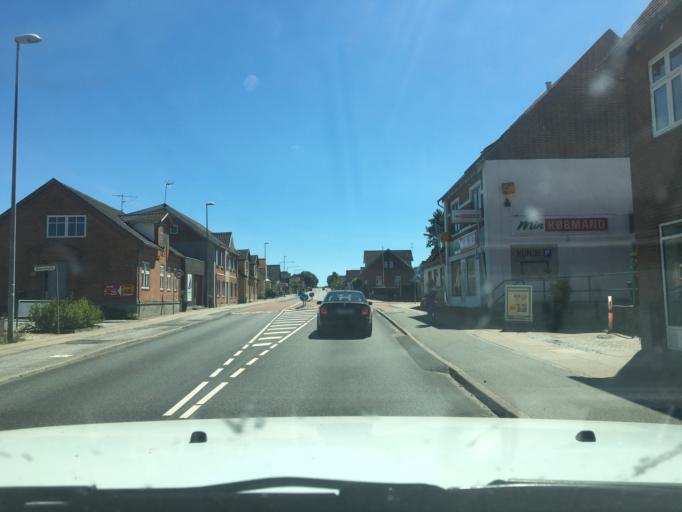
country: DK
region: Central Jutland
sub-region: Syddjurs Kommune
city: Hornslet
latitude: 56.3379
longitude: 10.3760
